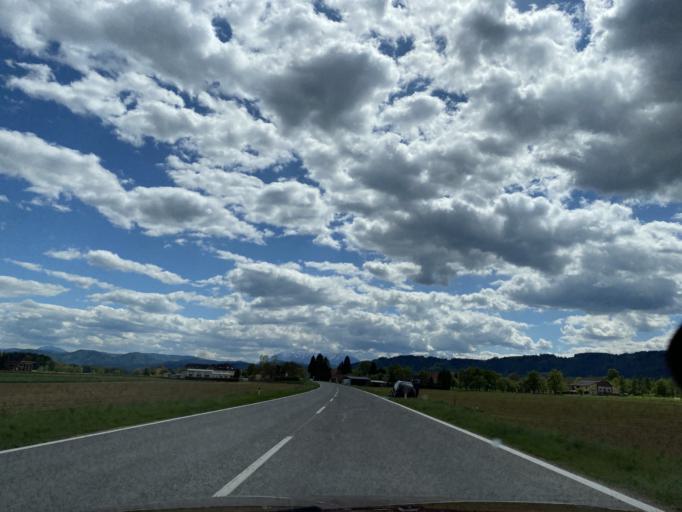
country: AT
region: Carinthia
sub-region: Politischer Bezirk Wolfsberg
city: Sankt Andrae
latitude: 46.7942
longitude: 14.8262
